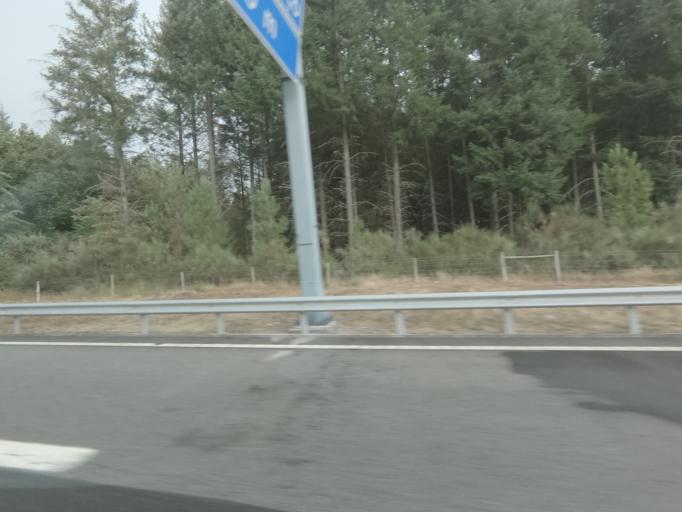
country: PT
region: Viseu
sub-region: Viseu
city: Abraveses
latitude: 40.6903
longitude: -7.9654
